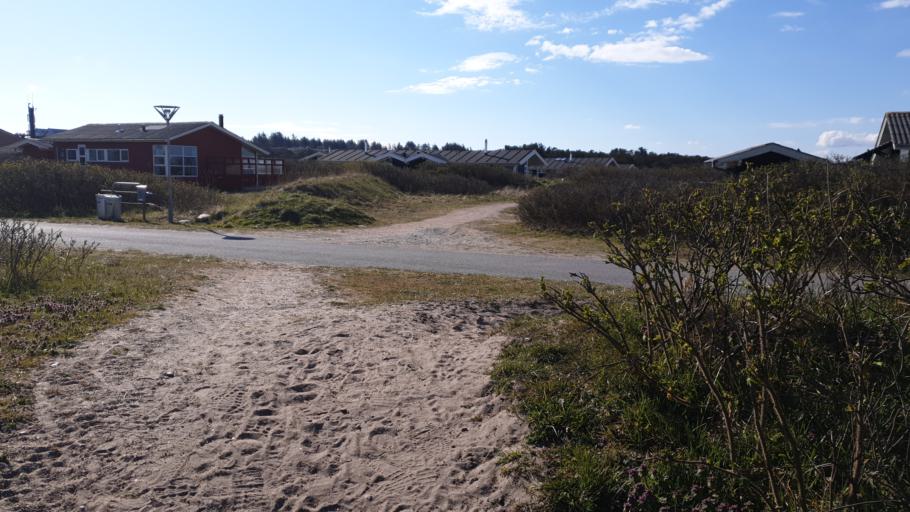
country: DK
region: North Denmark
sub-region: Hjorring Kommune
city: Hjorring
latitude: 57.4947
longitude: 9.8341
